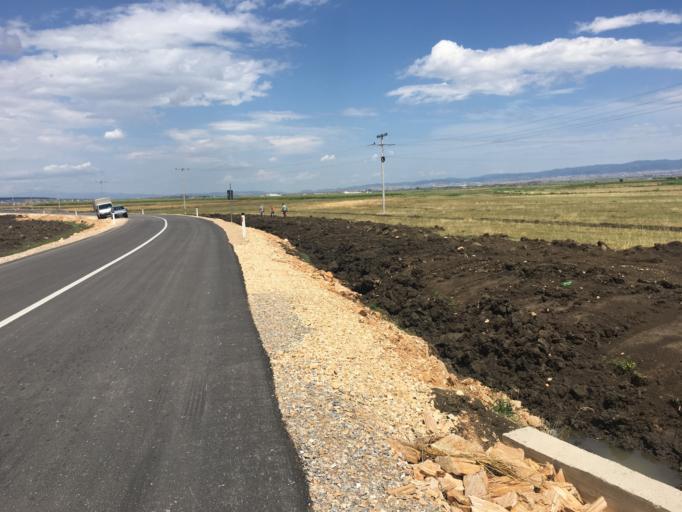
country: XK
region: Pristina
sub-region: Komuna e Gracanices
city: Glanica
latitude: 42.5457
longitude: 21.0208
